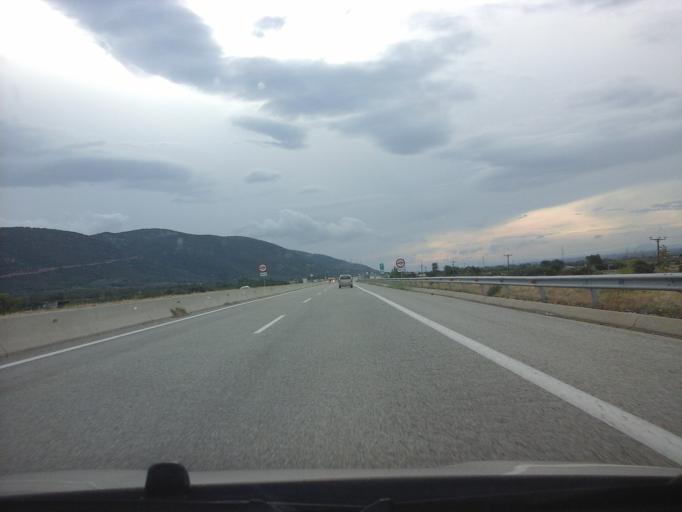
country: GR
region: East Macedonia and Thrace
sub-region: Nomos Xanthis
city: Selero
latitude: 41.1202
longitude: 25.0676
